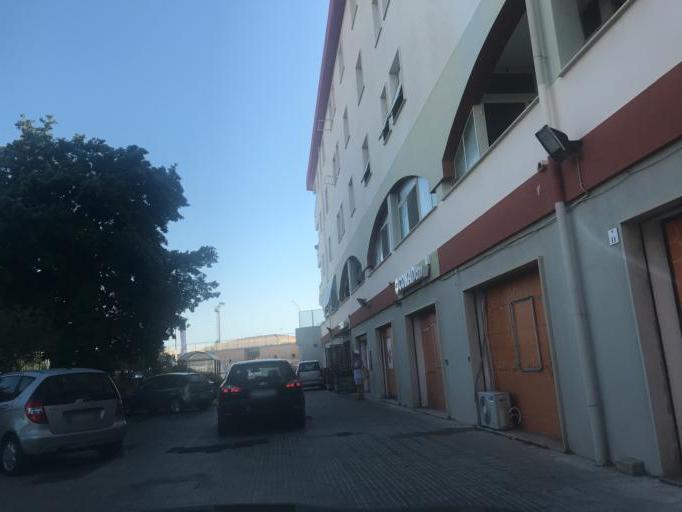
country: IT
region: Sardinia
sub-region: Provincia di Sassari
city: Alghero
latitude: 40.5499
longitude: 8.3268
